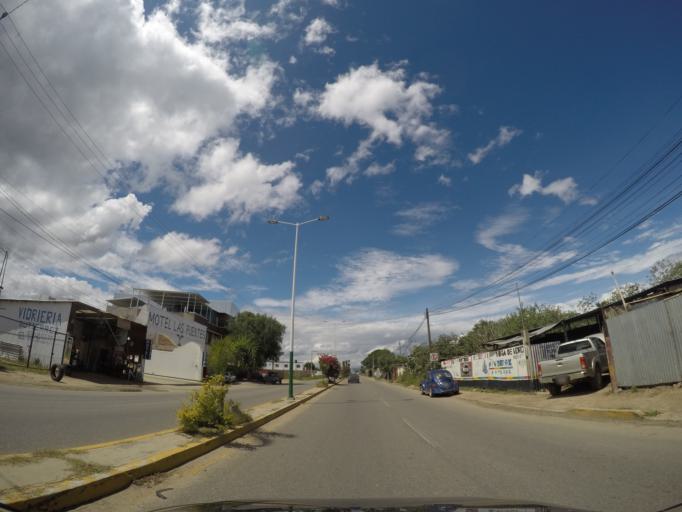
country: MX
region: Oaxaca
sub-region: Santa Cruz Xoxocotlan
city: Santa Cruz Xoxocotlan
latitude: 17.0214
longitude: -96.7308
